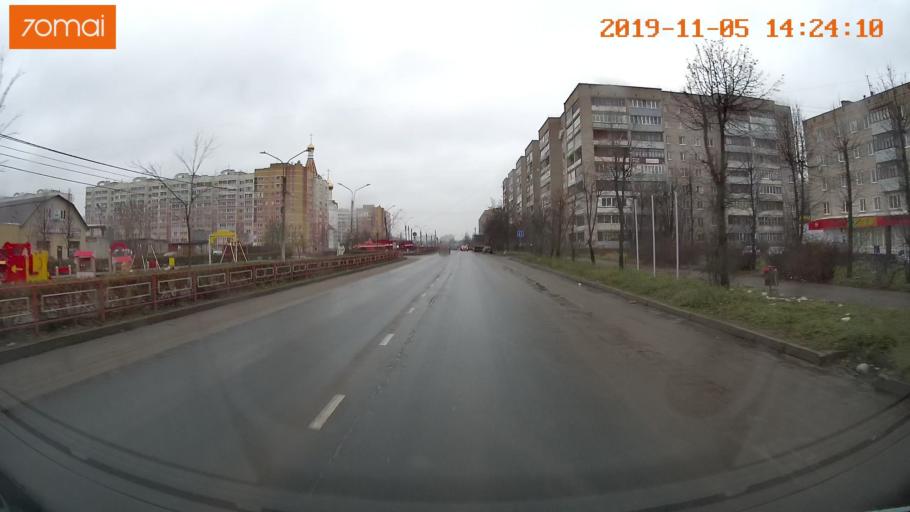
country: RU
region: Ivanovo
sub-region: Gorod Ivanovo
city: Ivanovo
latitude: 56.9671
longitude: 40.9994
